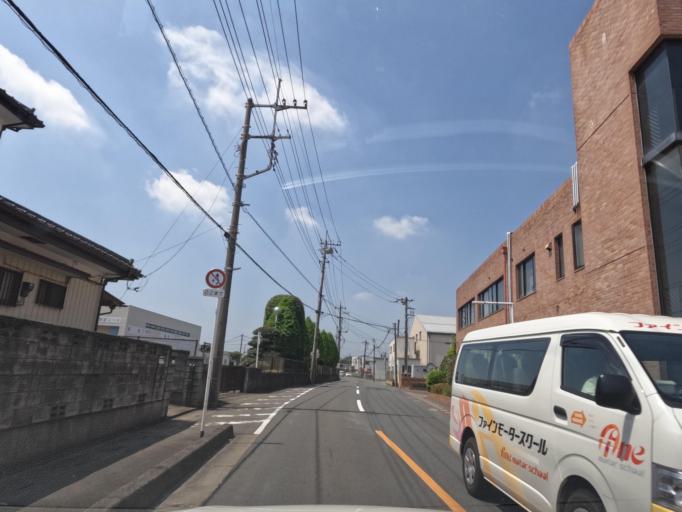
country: JP
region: Saitama
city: Ageoshimo
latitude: 35.9416
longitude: 139.5740
